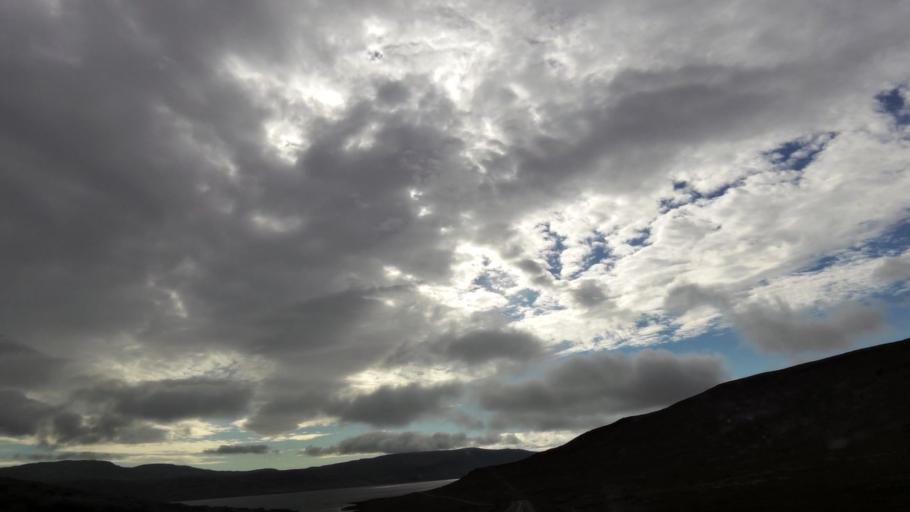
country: IS
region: West
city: Olafsvik
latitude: 65.5385
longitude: -23.8312
